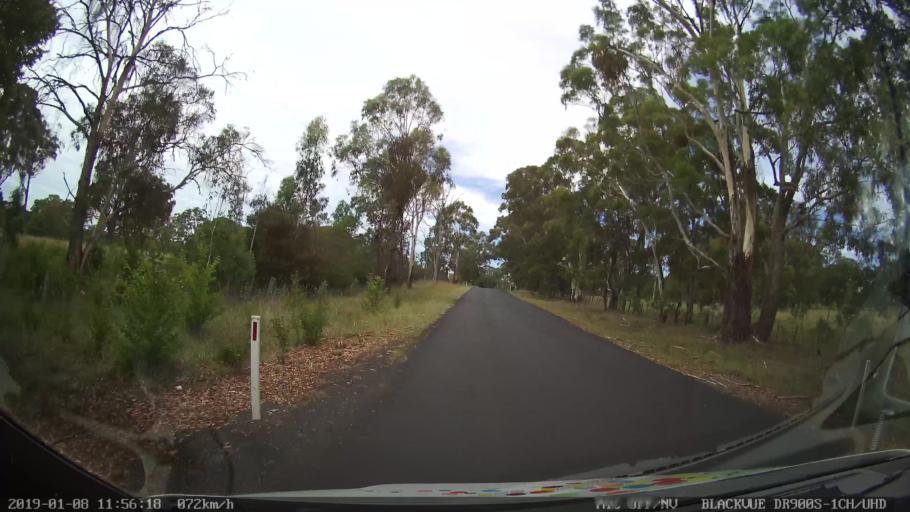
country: AU
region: New South Wales
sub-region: Armidale Dumaresq
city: Armidale
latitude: -30.4386
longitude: 151.5651
